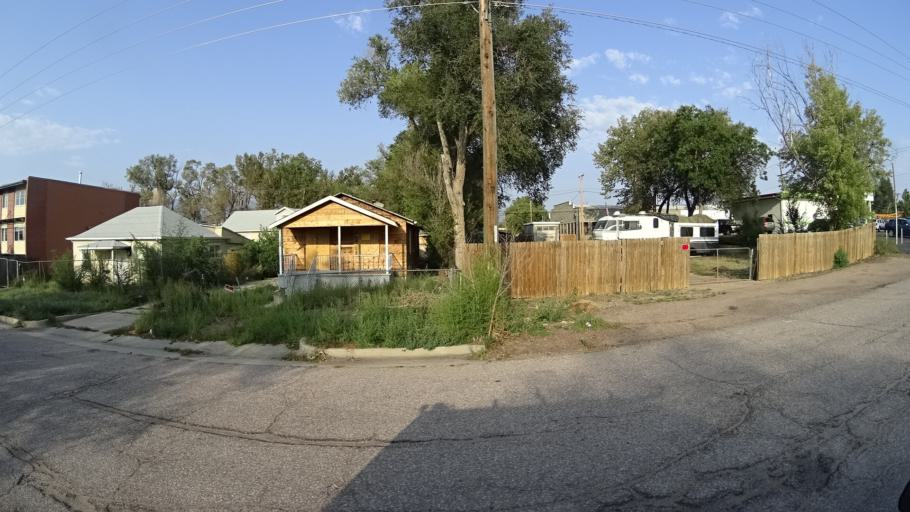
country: US
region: Colorado
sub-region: El Paso County
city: Colorado Springs
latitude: 38.8364
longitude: -104.7902
